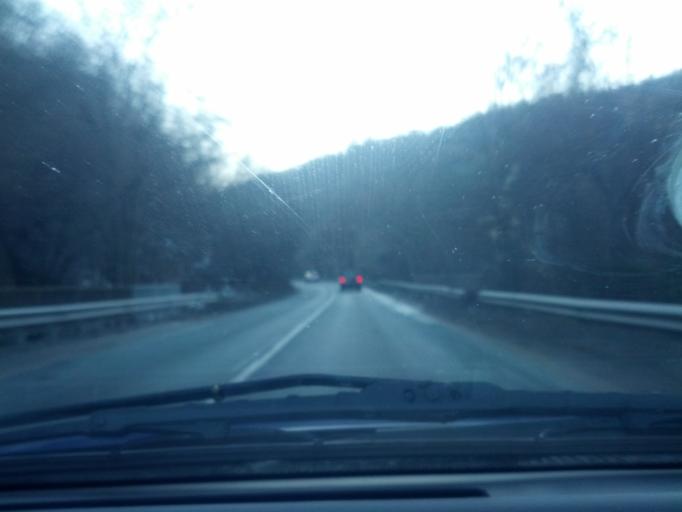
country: BG
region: Vratsa
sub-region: Obshtina Mezdra
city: Mezdra
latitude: 43.0421
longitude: 23.6698
